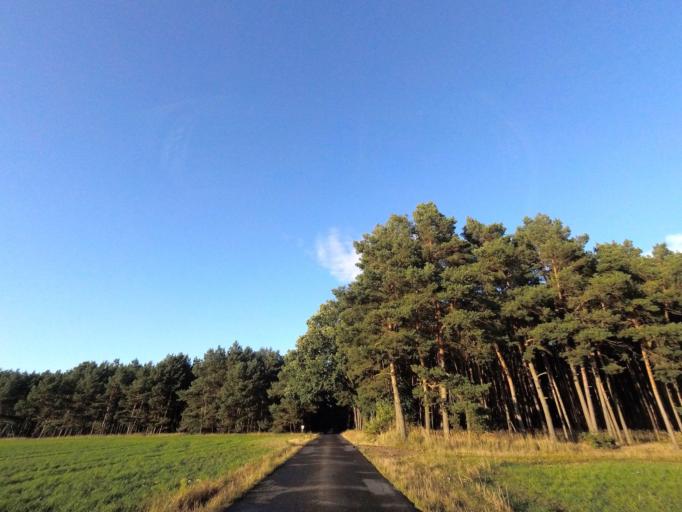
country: DE
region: Brandenburg
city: Treuenbrietzen
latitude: 52.0303
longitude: 12.8549
